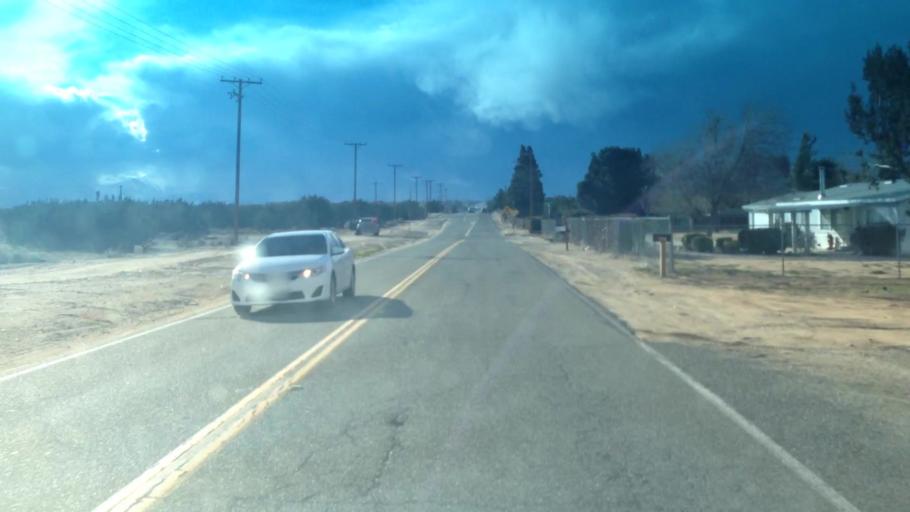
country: US
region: California
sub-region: San Bernardino County
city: Hesperia
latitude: 34.3837
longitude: -117.2867
